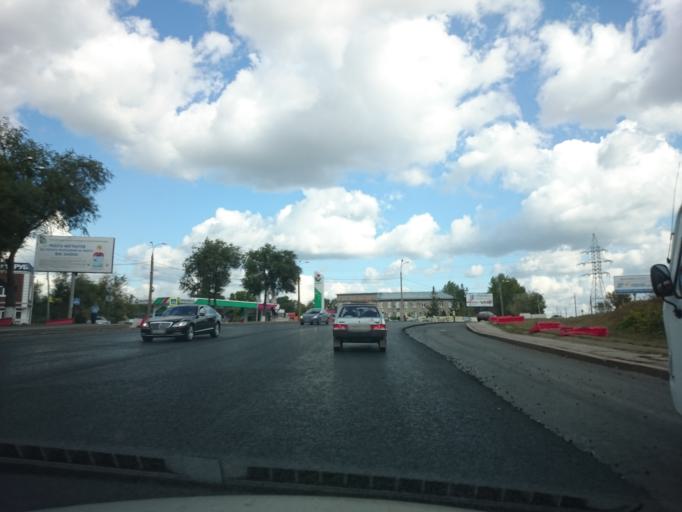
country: RU
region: Samara
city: Samara
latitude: 53.2215
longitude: 50.1653
